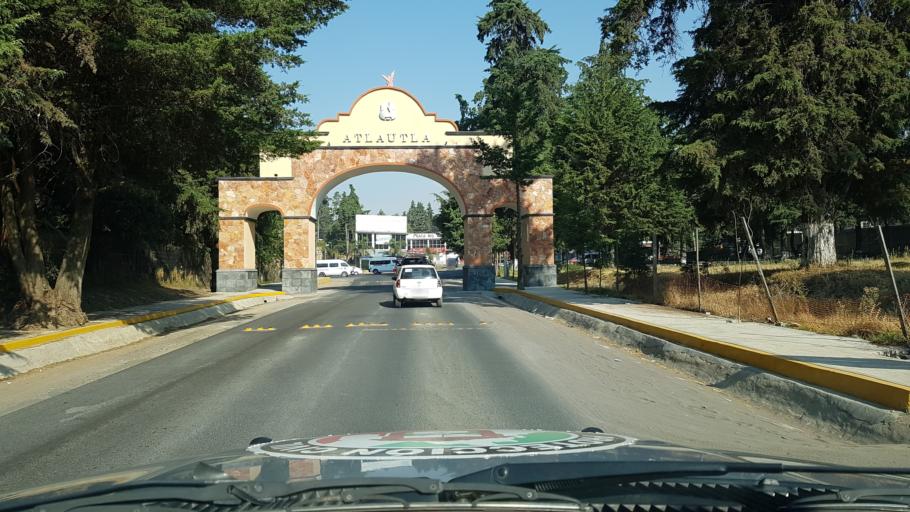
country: MX
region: Mexico
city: Ozumba de Alzate
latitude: 19.0549
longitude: -98.7870
